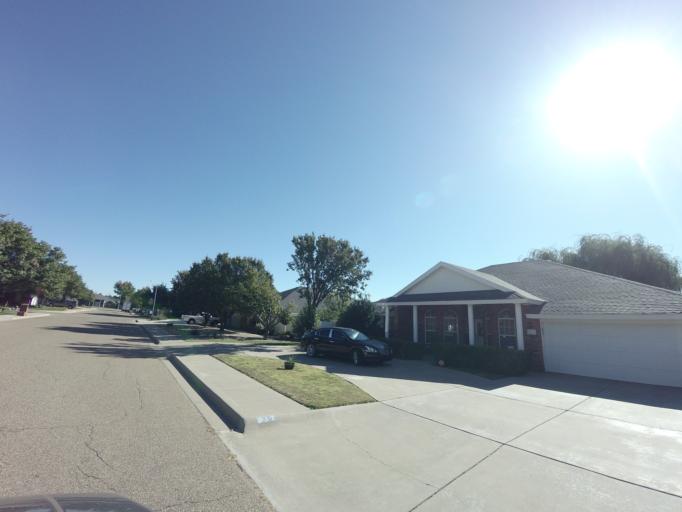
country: US
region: New Mexico
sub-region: Curry County
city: Clovis
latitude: 34.4243
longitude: -103.1728
